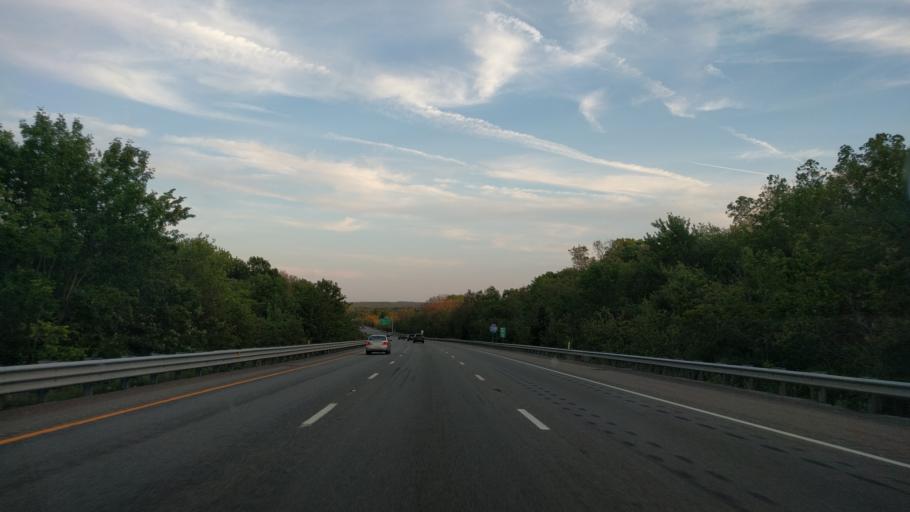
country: US
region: Massachusetts
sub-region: Worcester County
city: Cordaville
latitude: 42.2831
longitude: -71.5671
